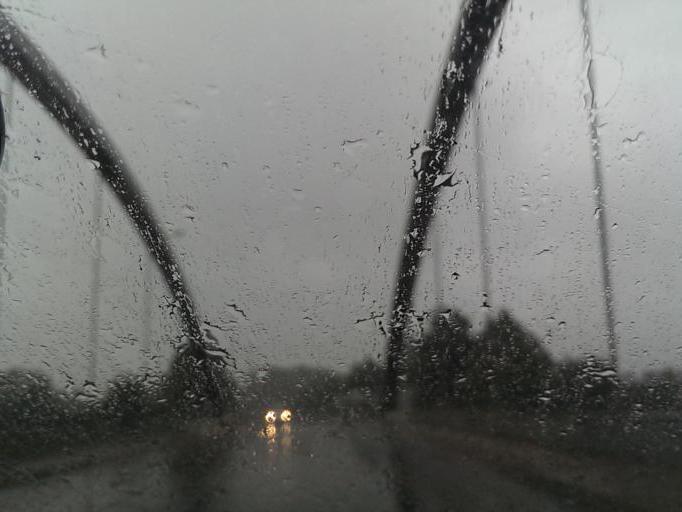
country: DE
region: Lower Saxony
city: Langenhagen
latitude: 52.4236
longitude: 9.6891
